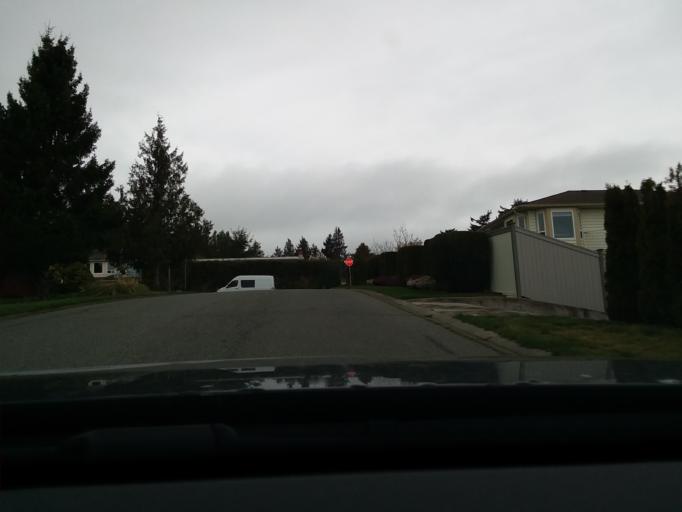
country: CA
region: British Columbia
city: North Saanich
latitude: 48.5596
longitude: -123.3967
